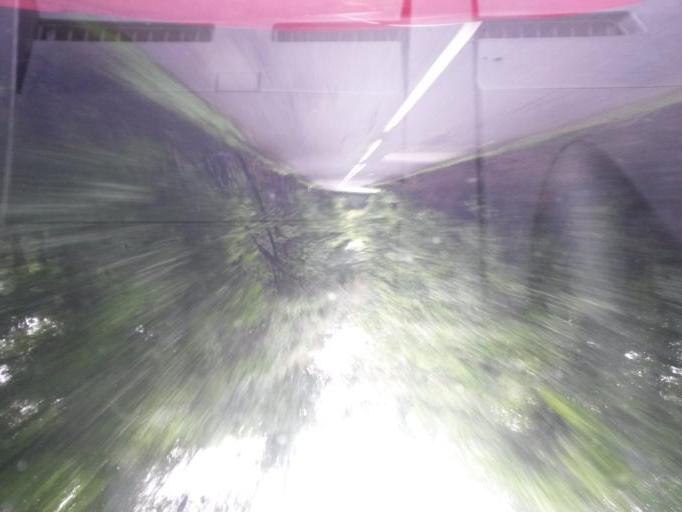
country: SK
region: Nitriansky
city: Sahy
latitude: 48.1680
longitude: 19.0165
